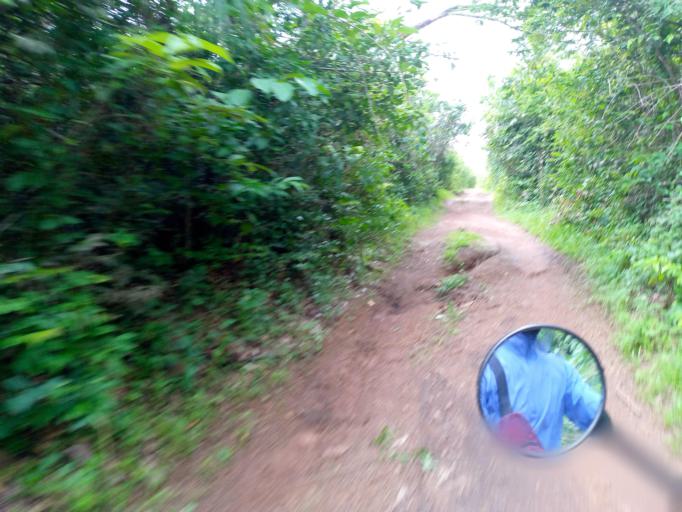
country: SL
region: Northern Province
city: Mange
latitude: 8.9812
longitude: -12.7378
